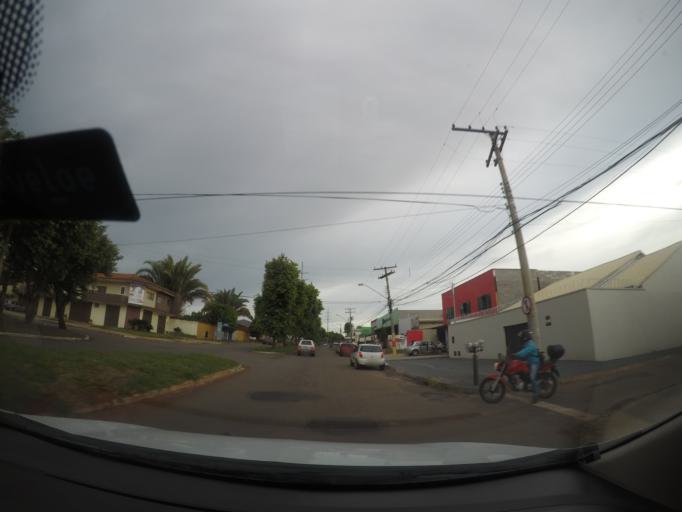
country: BR
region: Goias
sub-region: Goiania
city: Goiania
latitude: -16.7336
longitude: -49.3093
